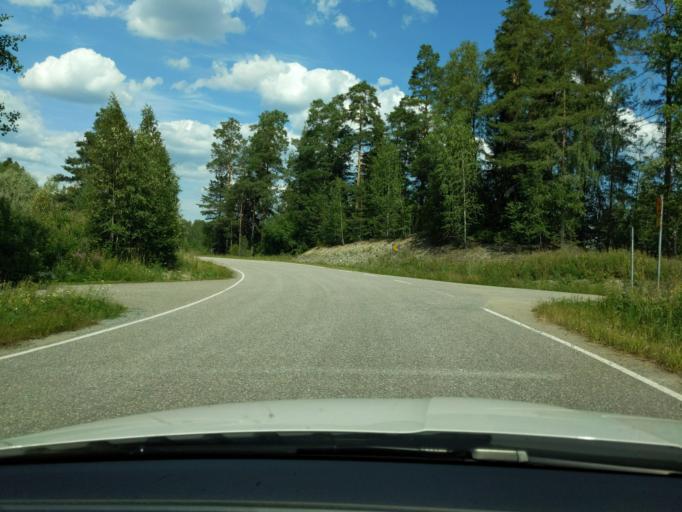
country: FI
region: Paijanne Tavastia
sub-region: Lahti
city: Heinola
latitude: 61.3362
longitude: 26.1720
